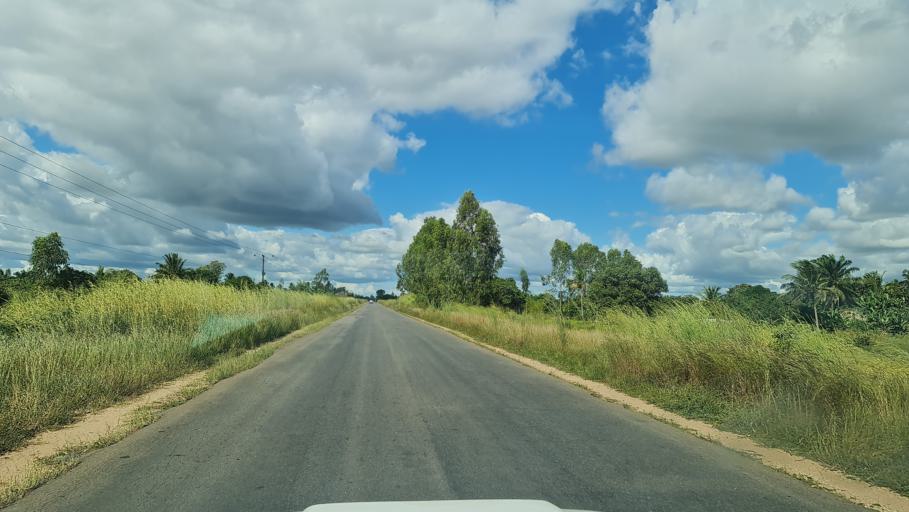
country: MZ
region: Zambezia
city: Quelimane
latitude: -17.5903
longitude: 36.7639
